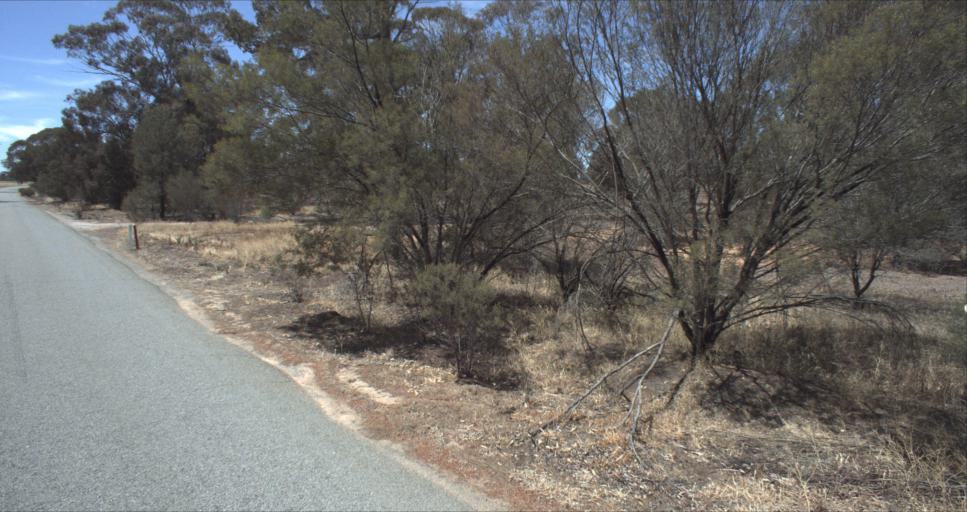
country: AU
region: New South Wales
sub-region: Leeton
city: Leeton
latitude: -34.6729
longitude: 146.4364
